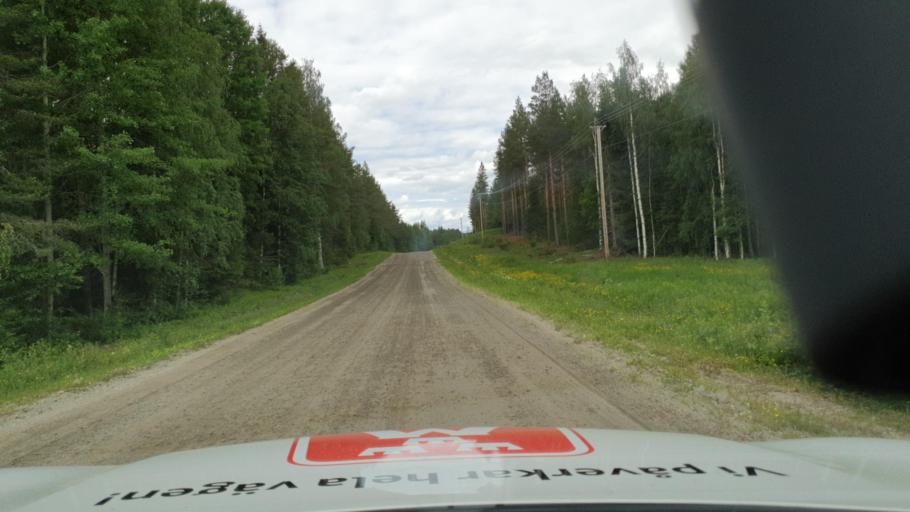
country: SE
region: Vaesterbotten
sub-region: Bjurholms Kommun
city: Bjurholm
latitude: 63.8496
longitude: 18.9845
